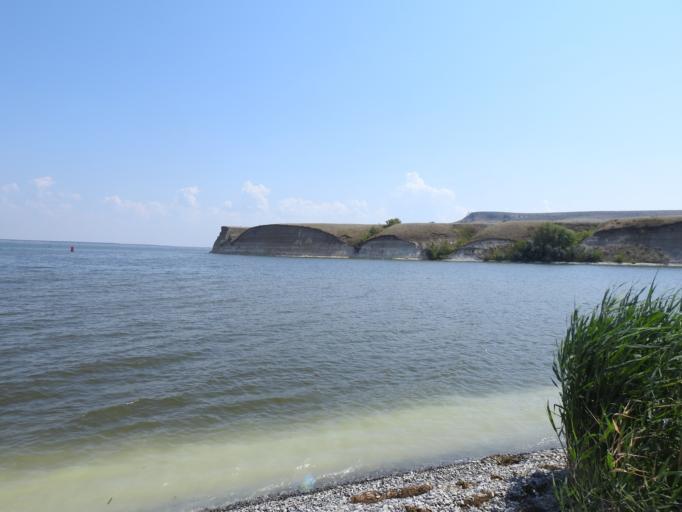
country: RU
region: Saratov
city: Kamenskiy
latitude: 50.5812
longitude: 45.7037
